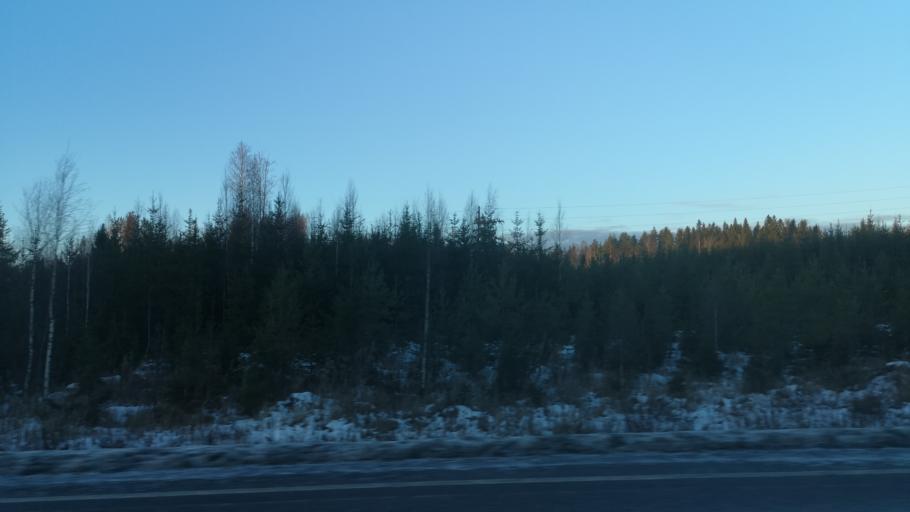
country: FI
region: Southern Savonia
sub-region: Savonlinna
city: Rantasalmi
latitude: 61.9560
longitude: 28.1713
